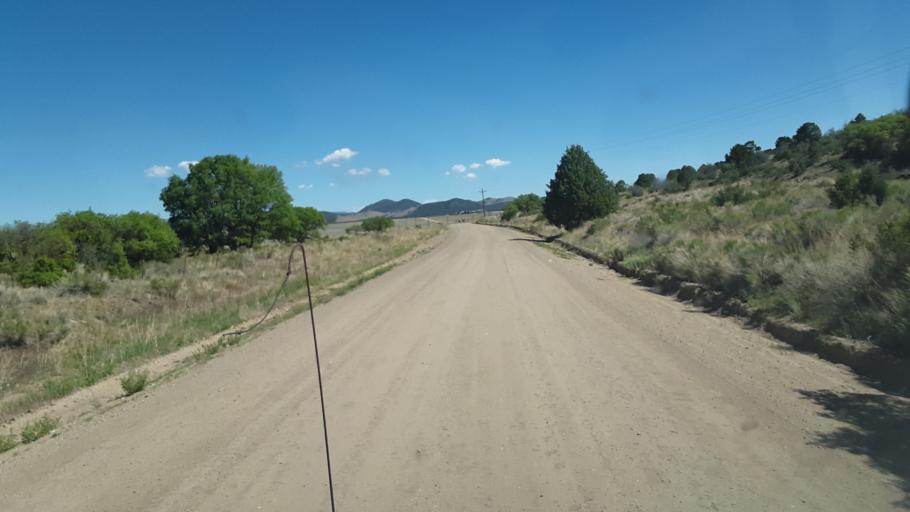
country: US
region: Colorado
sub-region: Custer County
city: Westcliffe
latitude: 38.2451
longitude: -105.5010
